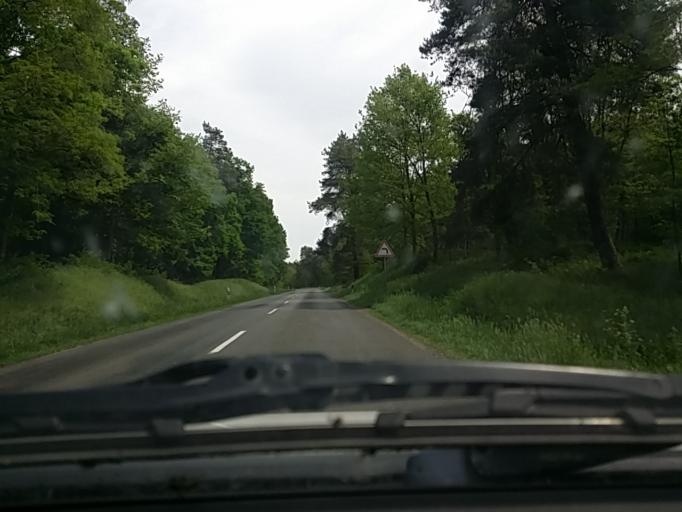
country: HU
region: Somogy
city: Barcs
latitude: 45.9645
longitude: 17.5147
